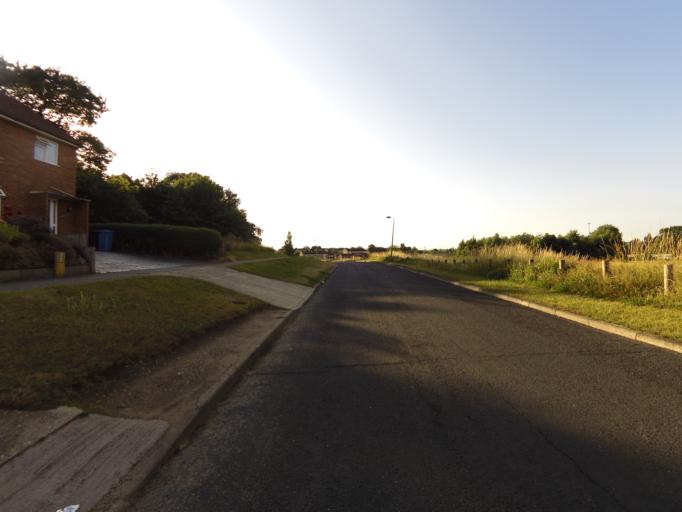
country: GB
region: England
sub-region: Suffolk
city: Ipswich
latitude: 52.0520
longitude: 1.1322
